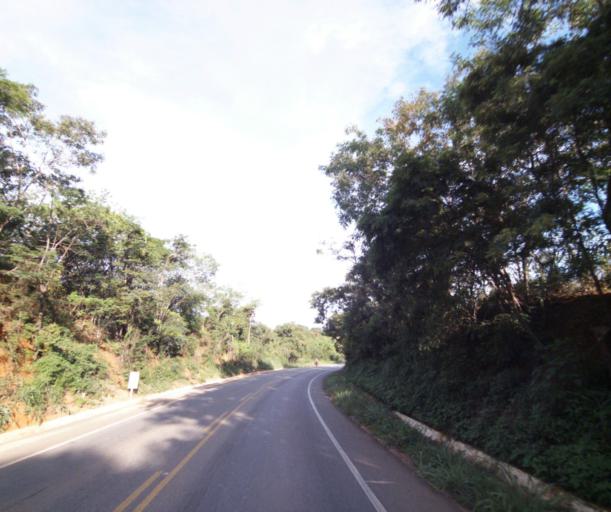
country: BR
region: Bahia
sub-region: Caetite
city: Caetite
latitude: -14.0667
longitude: -42.4678
